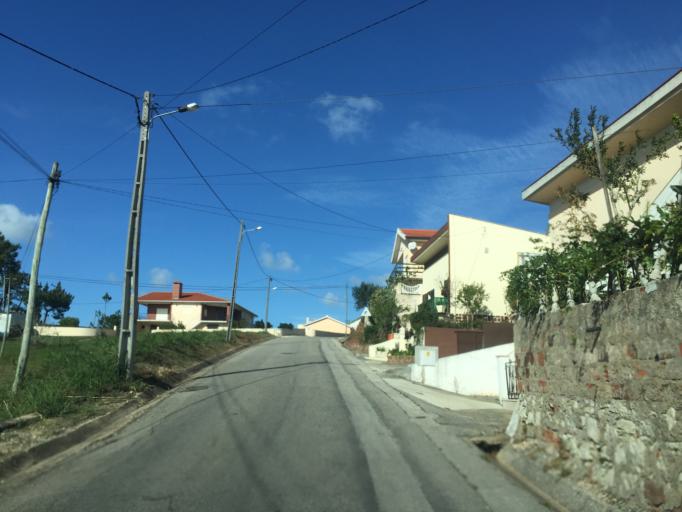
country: PT
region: Coimbra
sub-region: Figueira da Foz
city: Tavarede
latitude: 40.1711
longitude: -8.8395
